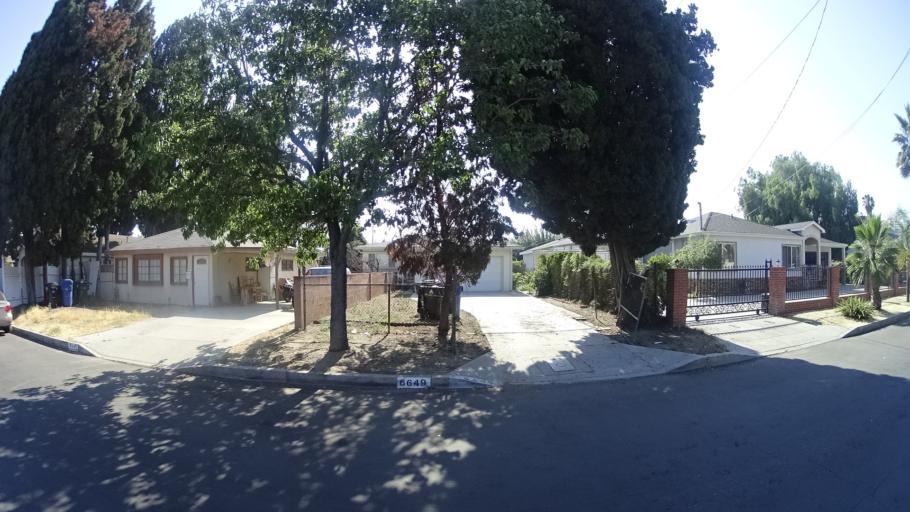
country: US
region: California
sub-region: Los Angeles County
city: Van Nuys
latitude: 34.1917
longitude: -118.4236
